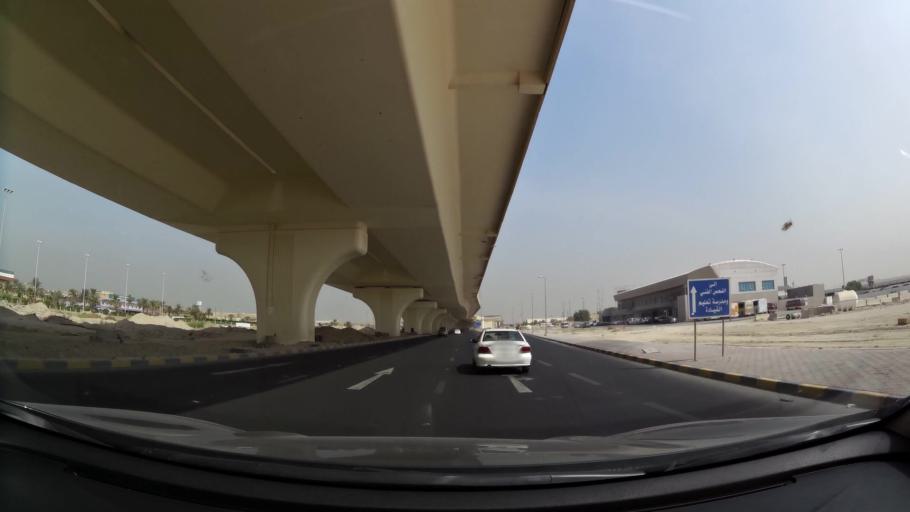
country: KW
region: Al Asimah
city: Ar Rabiyah
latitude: 29.3122
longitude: 47.8896
